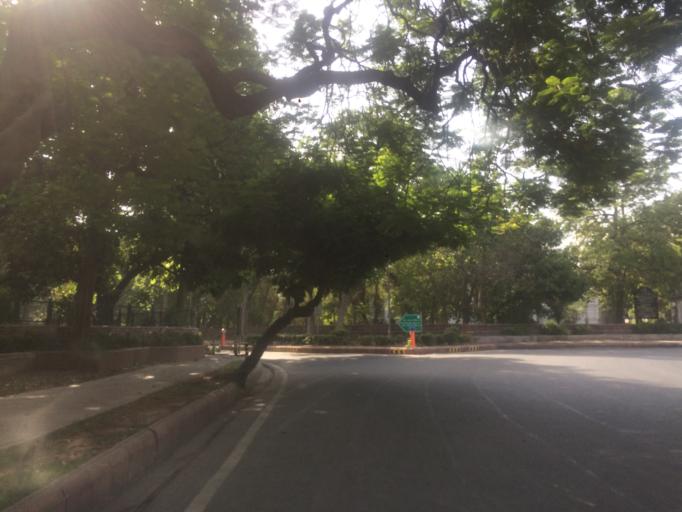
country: IN
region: NCT
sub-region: New Delhi
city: New Delhi
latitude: 28.6201
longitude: 77.2272
